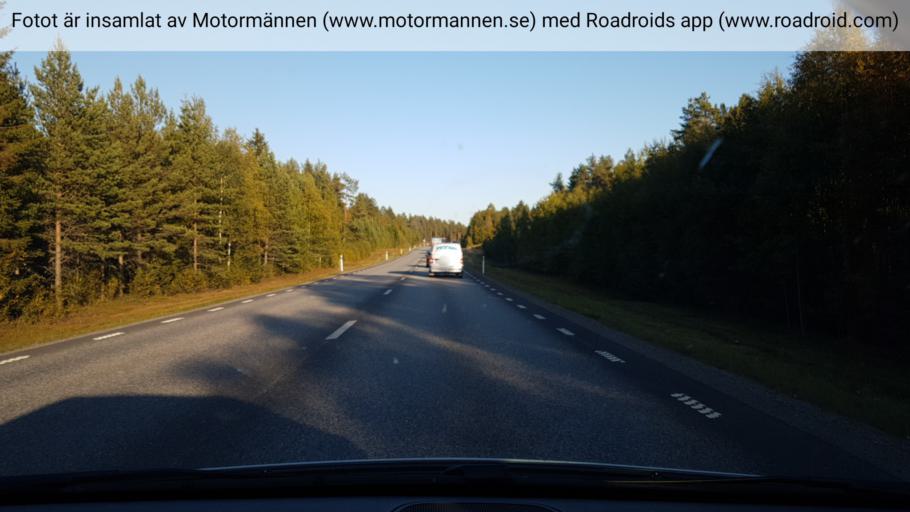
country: SE
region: Vaesterbotten
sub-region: Umea Kommun
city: Roback
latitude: 63.8472
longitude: 20.1429
